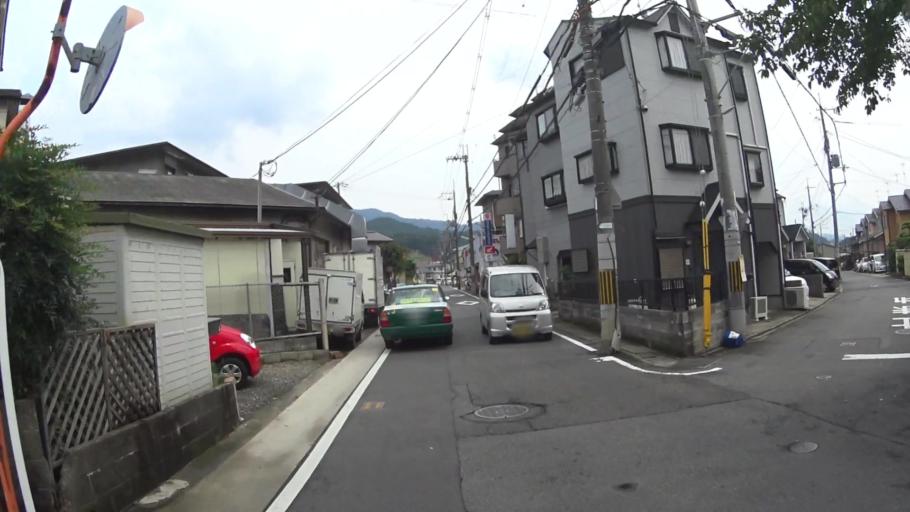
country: JP
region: Kyoto
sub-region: Kyoto-shi
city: Kamigyo-ku
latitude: 35.0732
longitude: 135.7907
